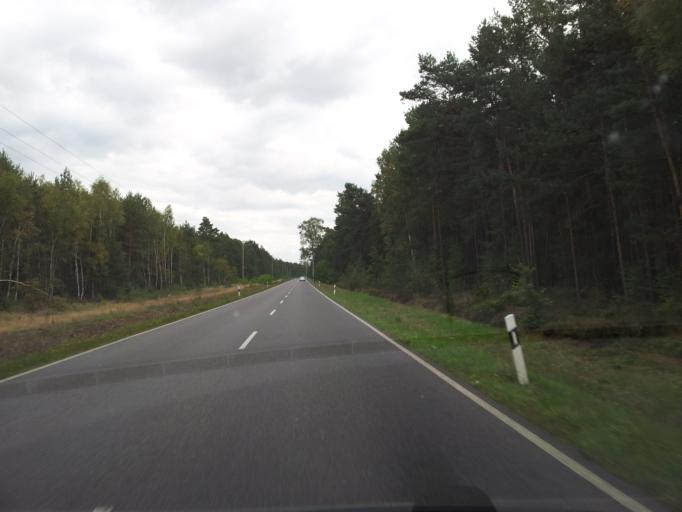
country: DE
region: Brandenburg
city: Guteborn
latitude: 51.4132
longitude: 13.9486
